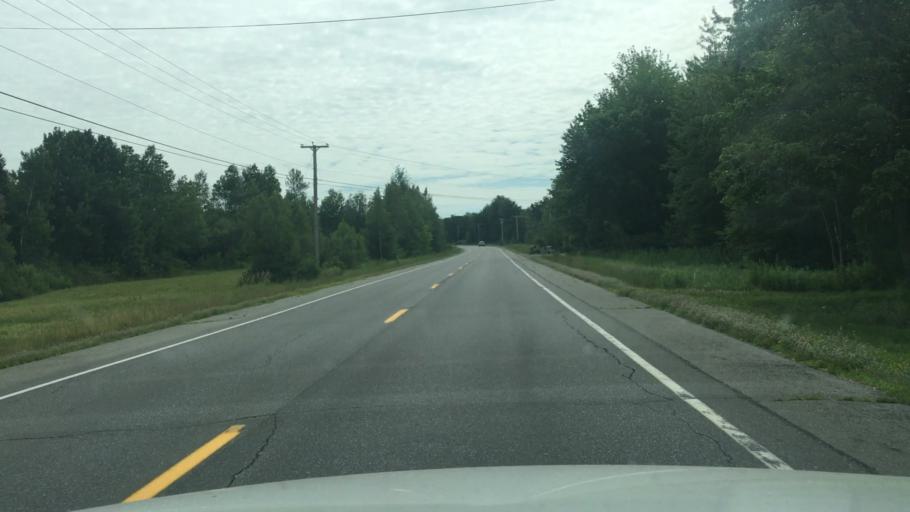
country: US
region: Maine
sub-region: Waldo County
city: Burnham
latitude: 44.6139
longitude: -69.3707
